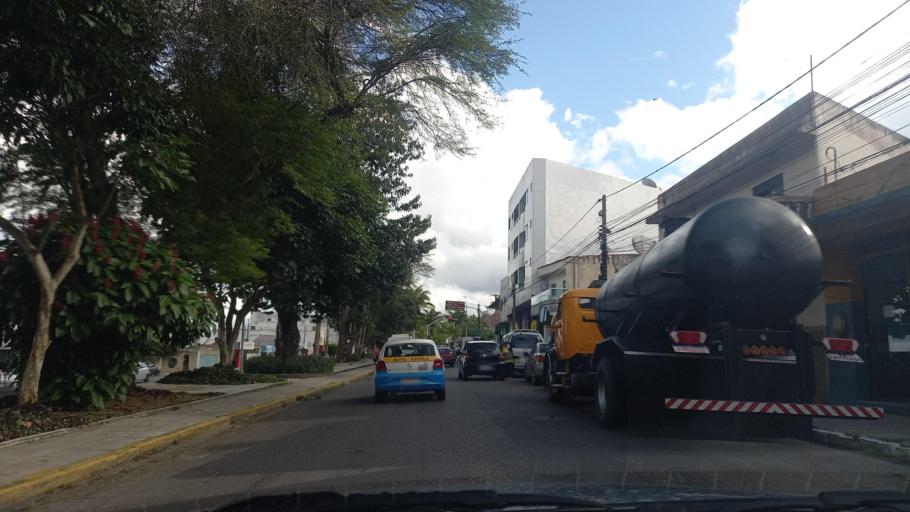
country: BR
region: Pernambuco
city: Garanhuns
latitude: -8.8855
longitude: -36.4895
